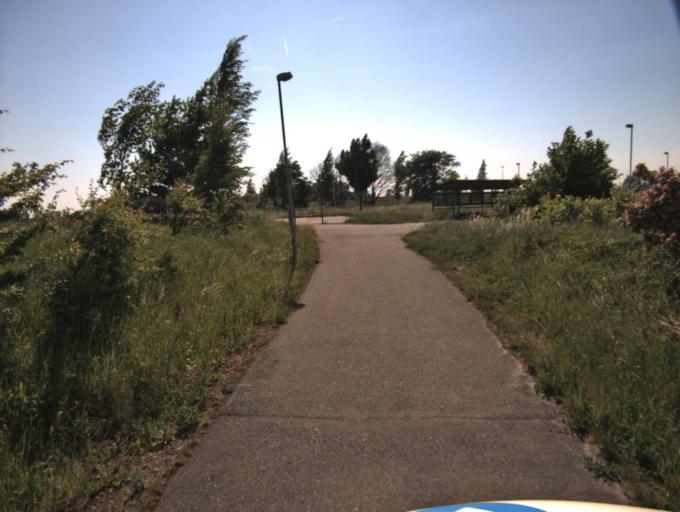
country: SE
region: Skane
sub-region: Kristianstads Kommun
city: Fjalkinge
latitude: 56.0340
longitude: 14.2698
